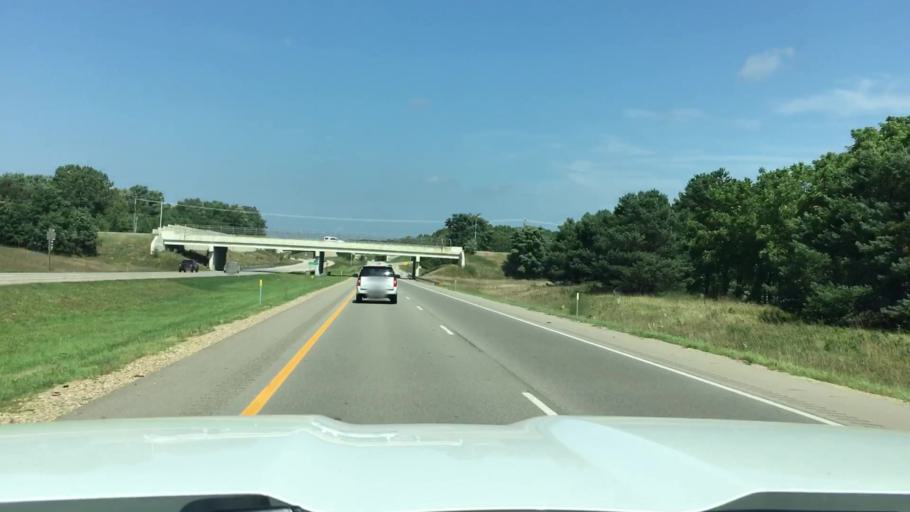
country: US
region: Michigan
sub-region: Kalamazoo County
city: Portage
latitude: 42.2285
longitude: -85.6390
